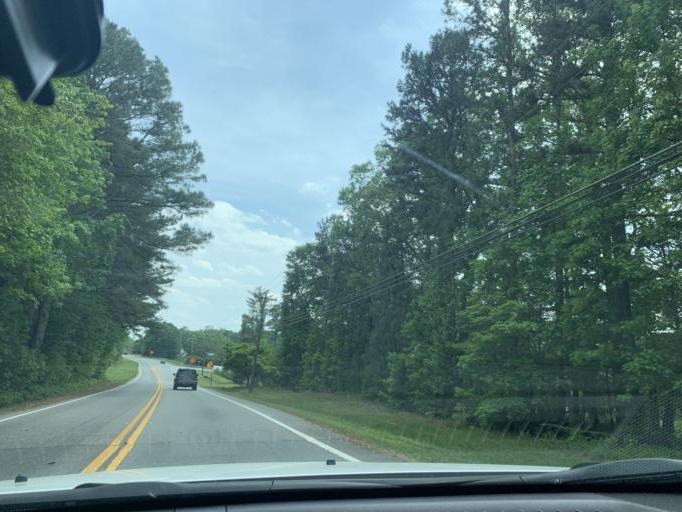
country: US
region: Georgia
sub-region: Forsyth County
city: Cumming
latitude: 34.1526
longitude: -84.1535
